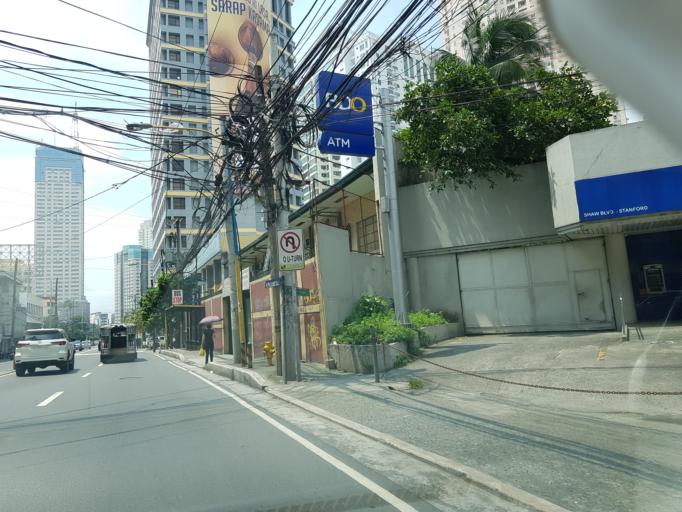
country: PH
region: Metro Manila
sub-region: Mandaluyong
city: Mandaluyong City
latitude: 14.5844
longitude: 121.0500
